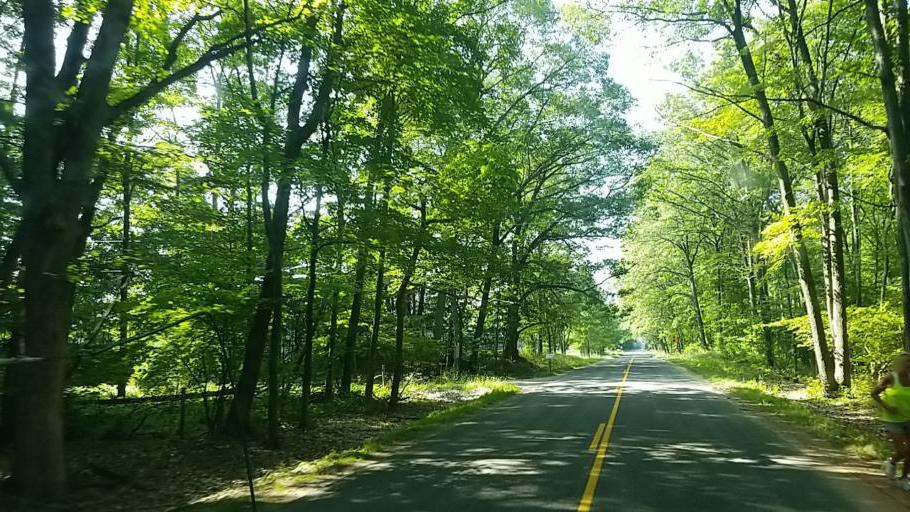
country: US
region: Michigan
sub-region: Muskegon County
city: Whitehall
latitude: 43.3595
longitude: -86.3764
